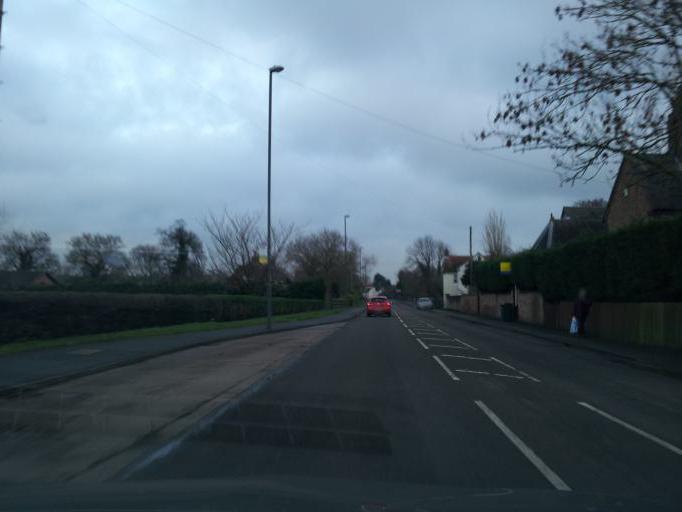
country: GB
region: England
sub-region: Derbyshire
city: Etwall
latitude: 52.8730
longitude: -1.6453
